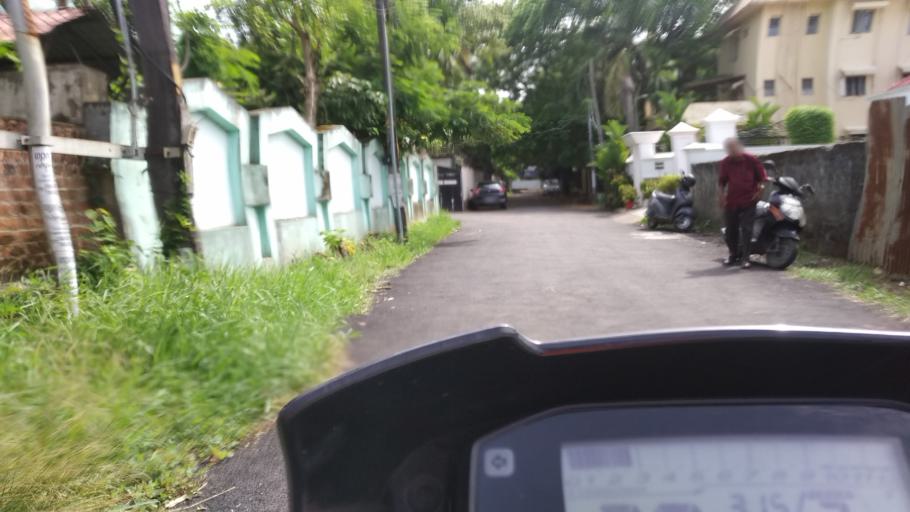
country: IN
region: Kerala
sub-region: Ernakulam
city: Cochin
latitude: 9.9807
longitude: 76.2926
